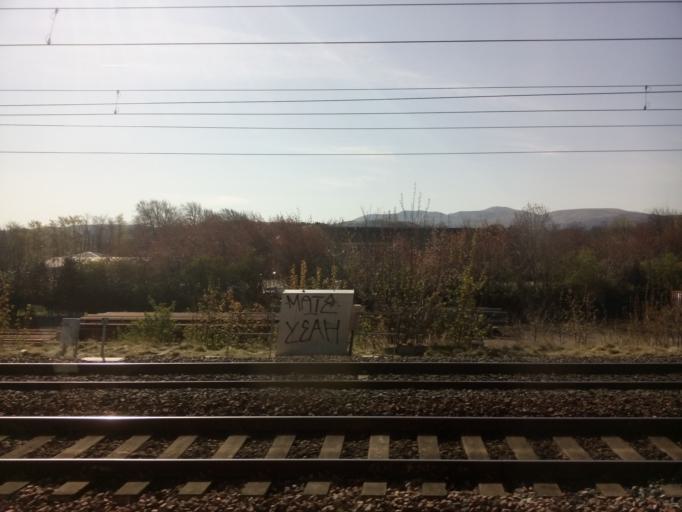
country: GB
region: Scotland
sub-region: Edinburgh
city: Colinton
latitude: 55.9388
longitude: -3.2482
